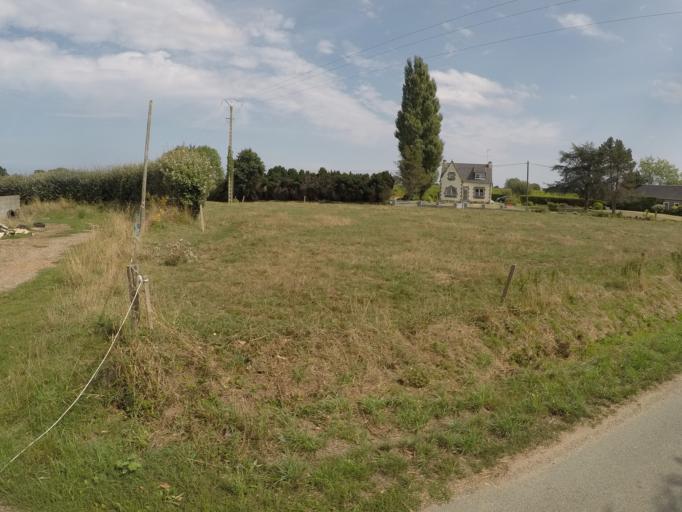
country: FR
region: Brittany
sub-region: Departement des Cotes-d'Armor
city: Goudelin
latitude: 48.5973
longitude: -3.0254
